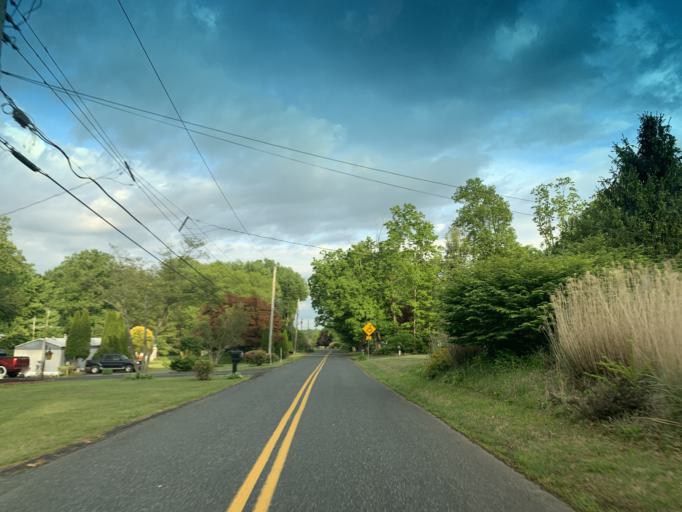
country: US
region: Pennsylvania
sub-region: York County
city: Susquehanna Trails
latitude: 39.6750
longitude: -76.2396
